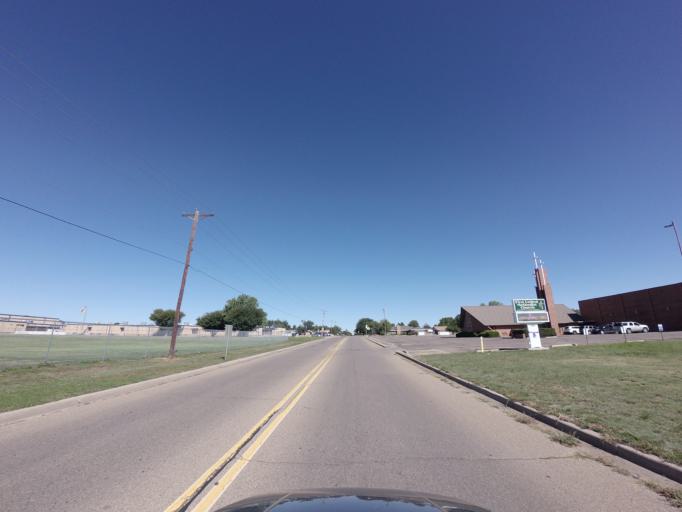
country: US
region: New Mexico
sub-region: Curry County
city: Clovis
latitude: 34.4132
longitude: -103.1877
